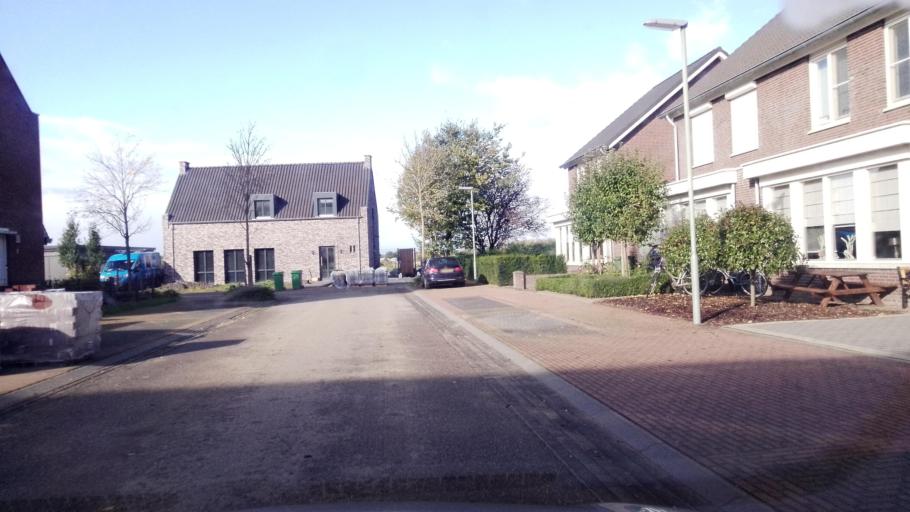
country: NL
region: Limburg
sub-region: Gemeente Venlo
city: Arcen
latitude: 51.4492
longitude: 6.1683
